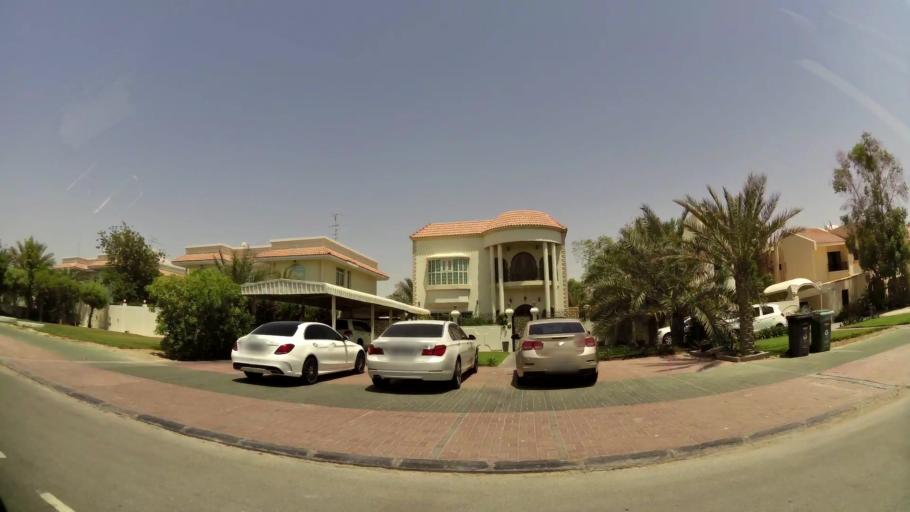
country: AE
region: Dubai
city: Dubai
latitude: 25.1860
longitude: 55.2349
